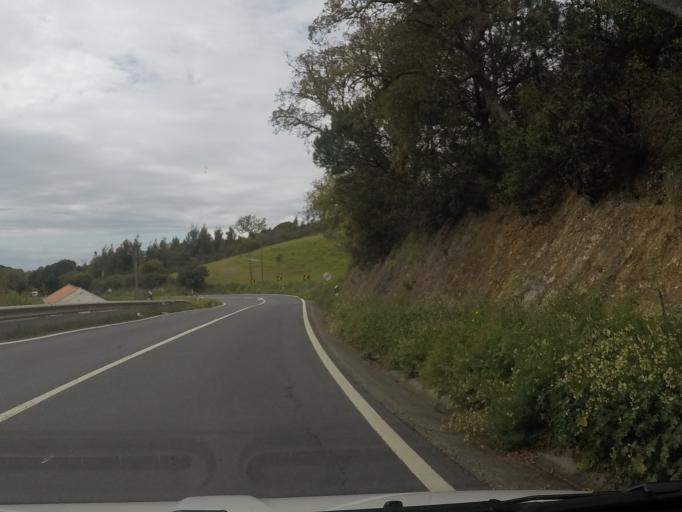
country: PT
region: Setubal
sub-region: Sines
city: Porto Covo
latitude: 37.8676
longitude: -8.7360
